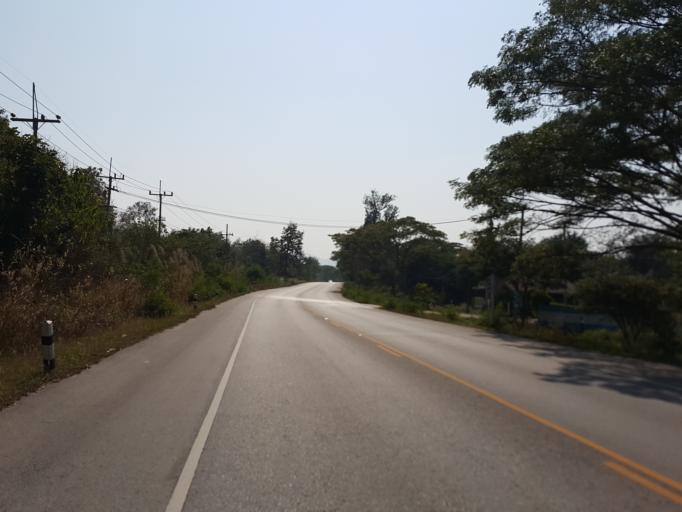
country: TH
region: Lampang
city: Mueang Pan
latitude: 18.8180
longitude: 99.5947
